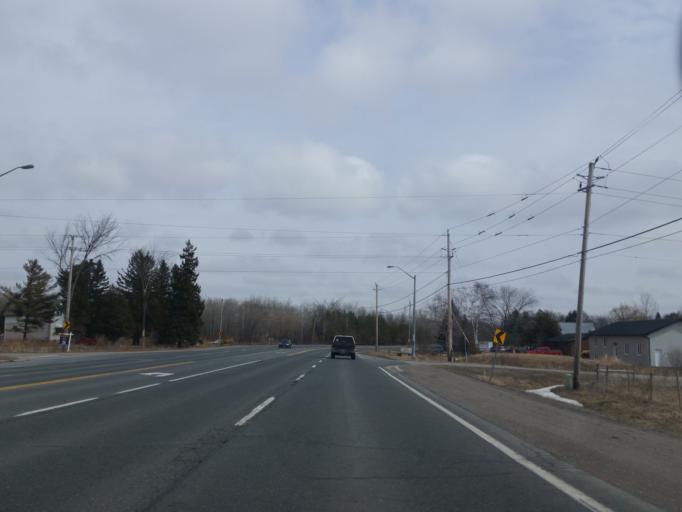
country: CA
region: Ontario
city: Oshawa
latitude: 43.9136
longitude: -78.7578
